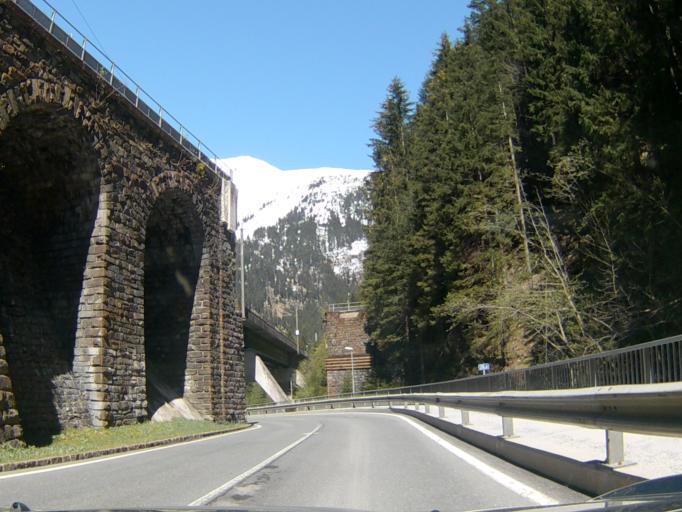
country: AT
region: Salzburg
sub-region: Politischer Bezirk Sankt Johann im Pongau
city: Bad Gastein
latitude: 47.0836
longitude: 13.1262
